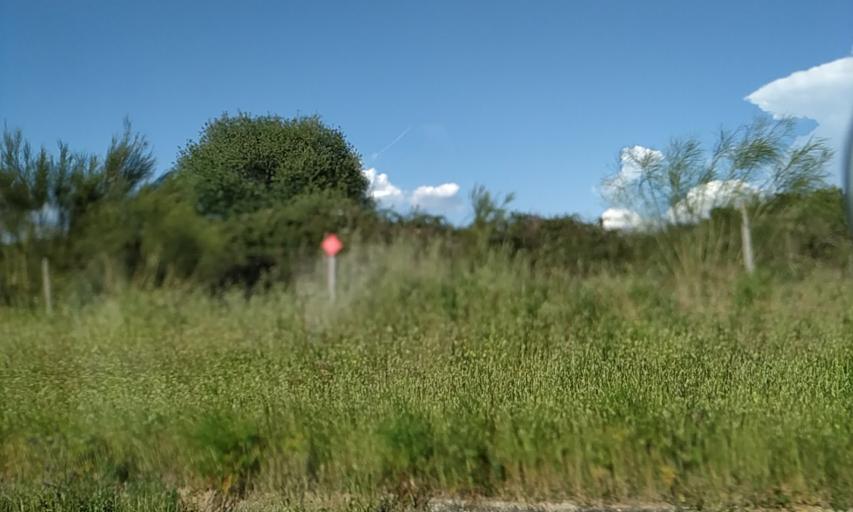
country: PT
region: Portalegre
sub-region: Portalegre
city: Urra
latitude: 39.0816
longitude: -7.4372
